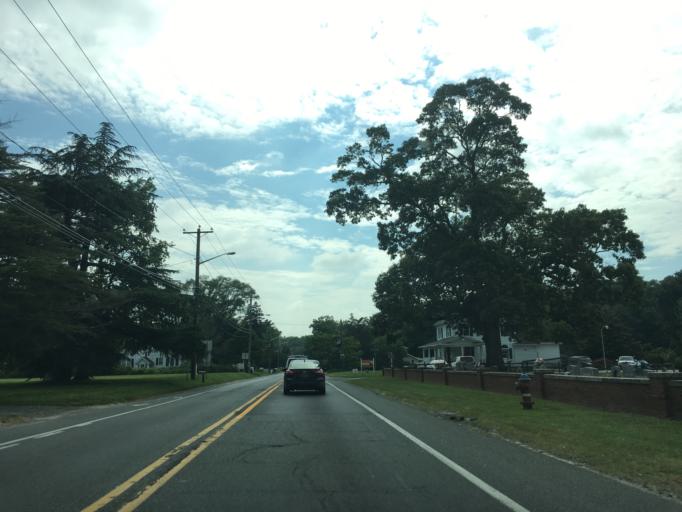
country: US
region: Delaware
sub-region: Sussex County
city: Millsboro
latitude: 38.5479
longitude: -75.2386
